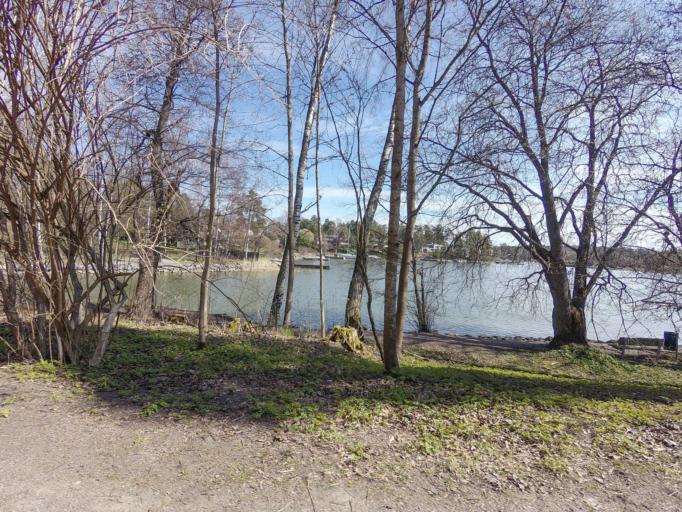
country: FI
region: Uusimaa
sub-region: Helsinki
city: Vantaa
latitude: 60.1867
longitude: 25.0598
